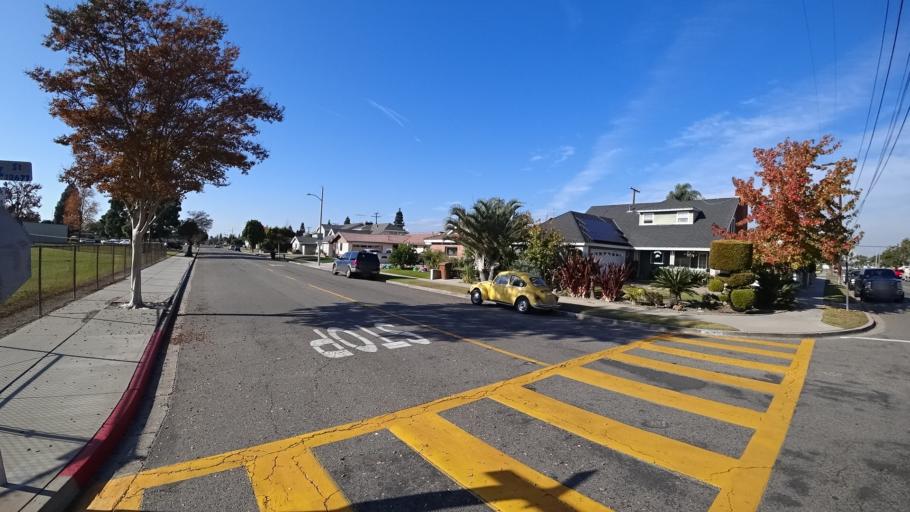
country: US
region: California
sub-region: Orange County
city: Westminster
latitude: 33.7785
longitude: -118.0241
